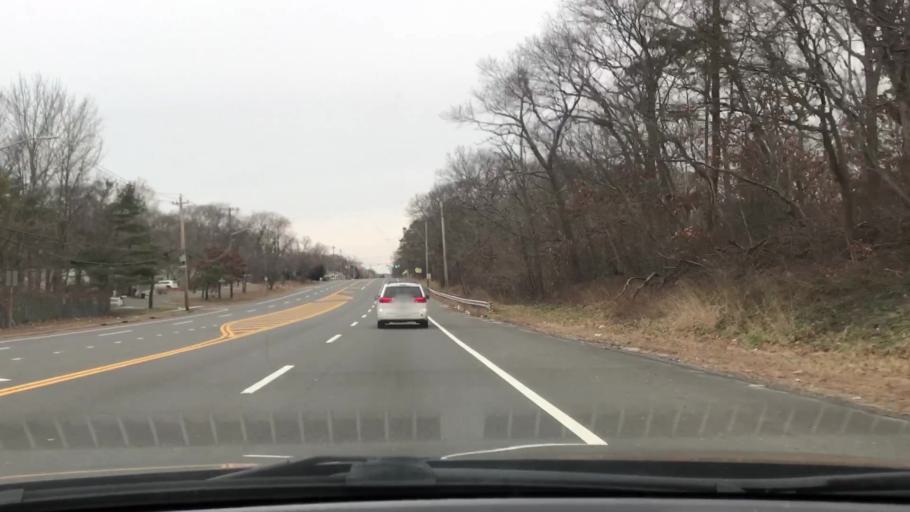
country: US
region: New York
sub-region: Suffolk County
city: North Patchogue
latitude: 40.7843
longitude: -73.0161
